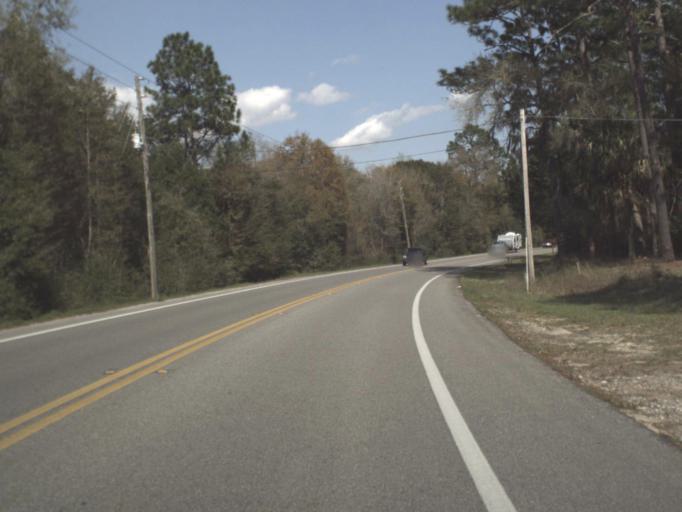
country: US
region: Florida
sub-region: Wakulla County
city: Crawfordville
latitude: 30.0714
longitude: -84.4474
